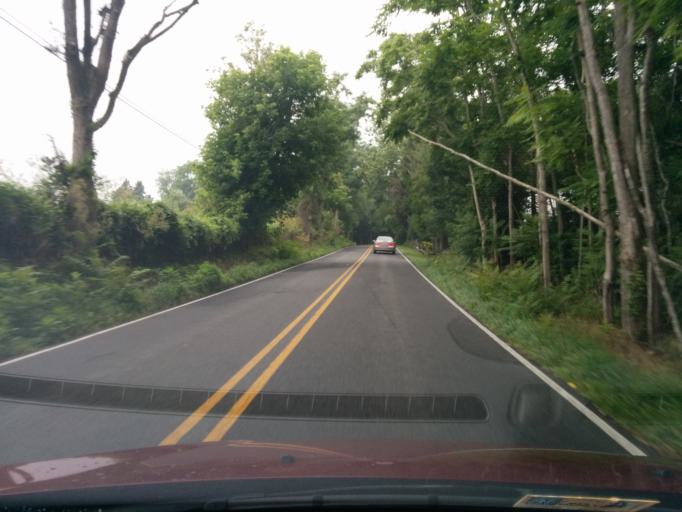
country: US
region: Virginia
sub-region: Rockbridge County
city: East Lexington
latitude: 37.8180
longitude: -79.4241
